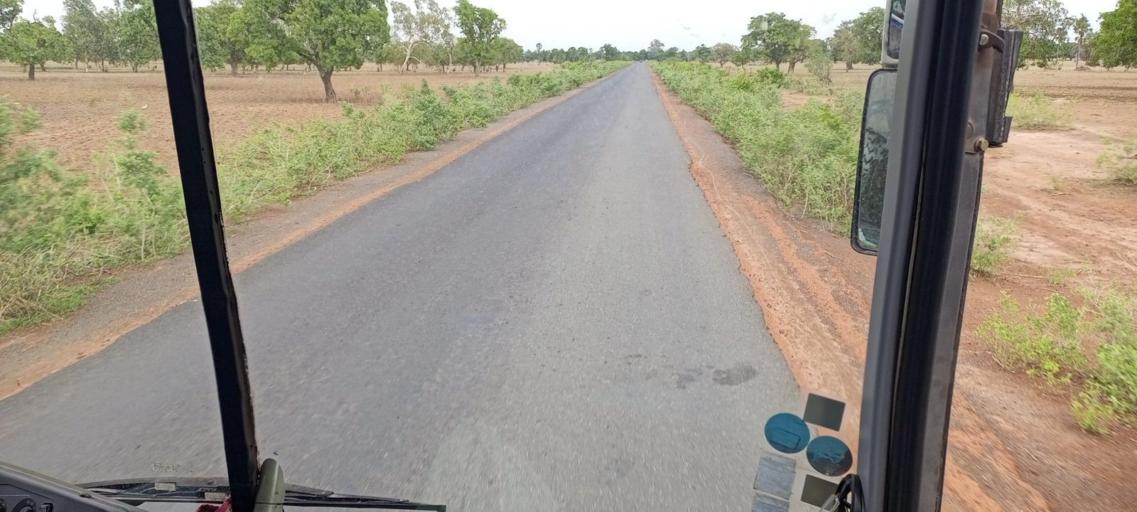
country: ML
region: Segou
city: Bla
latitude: 12.7451
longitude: -5.7307
